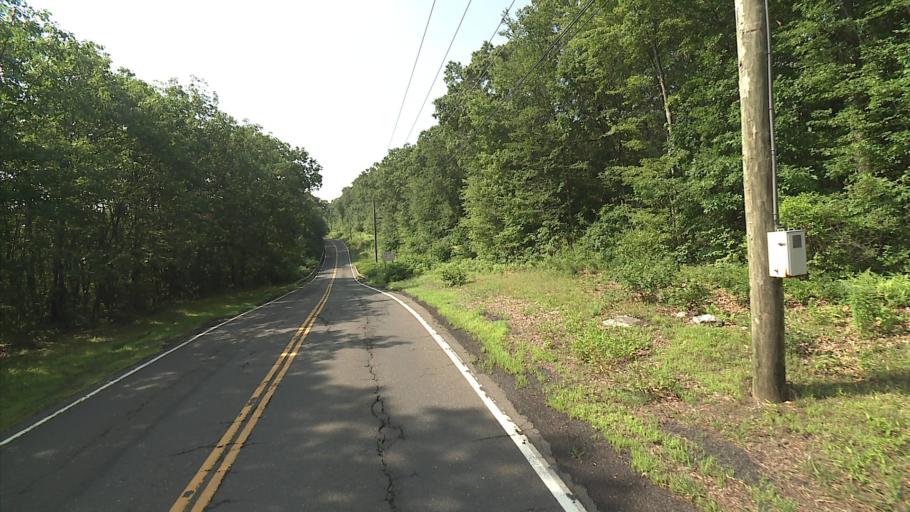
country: US
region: Connecticut
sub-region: New Haven County
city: Wolcott
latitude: 41.5817
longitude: -72.9522
